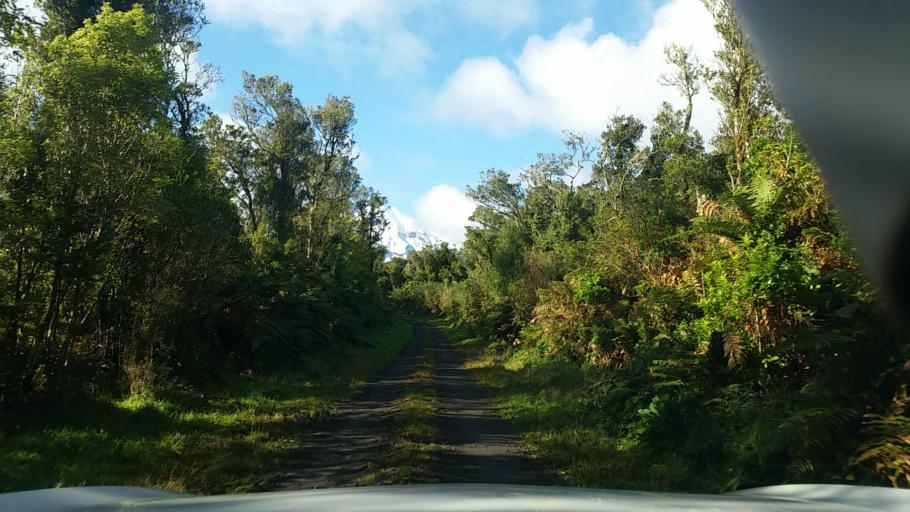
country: NZ
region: Taranaki
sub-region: South Taranaki District
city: Opunake
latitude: -39.2502
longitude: 173.9426
